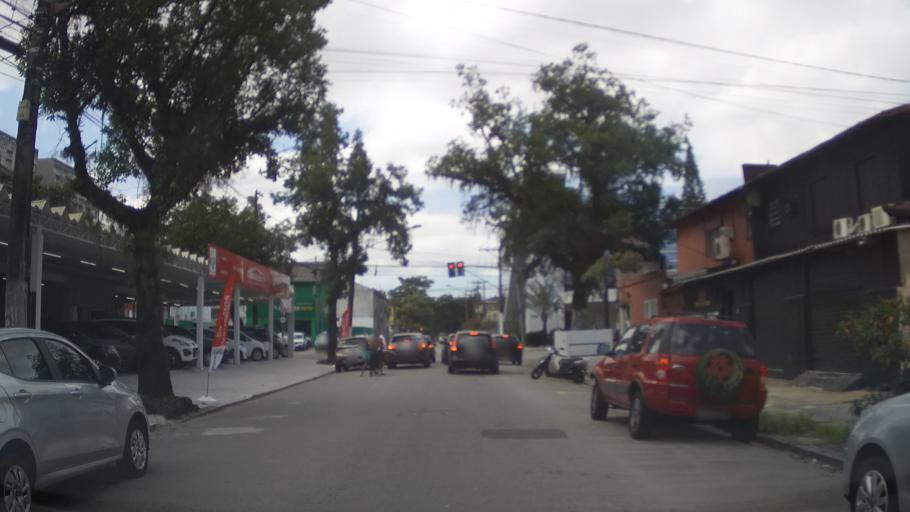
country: BR
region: Sao Paulo
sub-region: Santos
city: Santos
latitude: -23.9491
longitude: -46.3227
